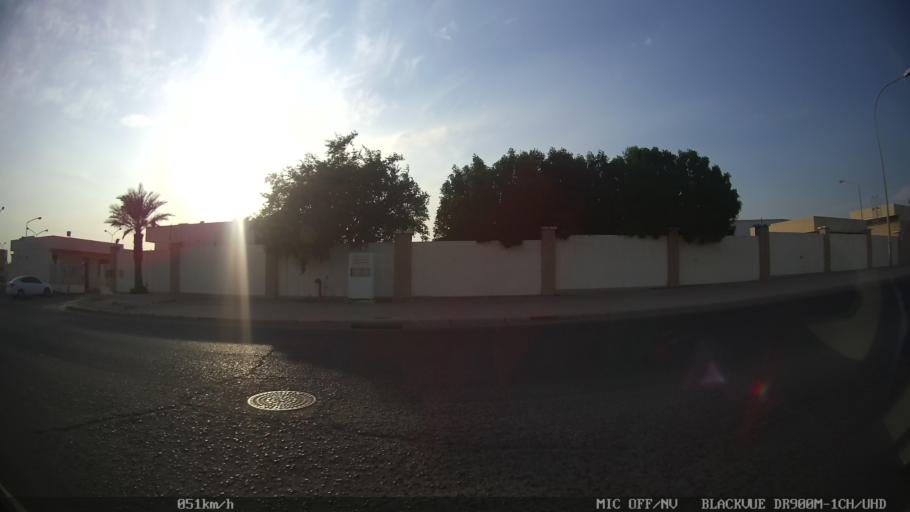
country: KW
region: Al Farwaniyah
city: Janub as Surrah
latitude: 29.2355
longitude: 48.0094
